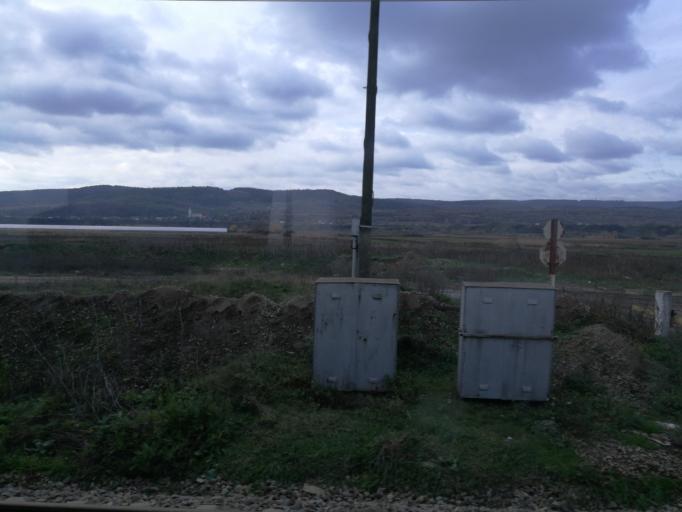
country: RO
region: Bacau
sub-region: Comuna Racaciuni
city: Gheorghe Doja
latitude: 46.3982
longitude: 26.9631
